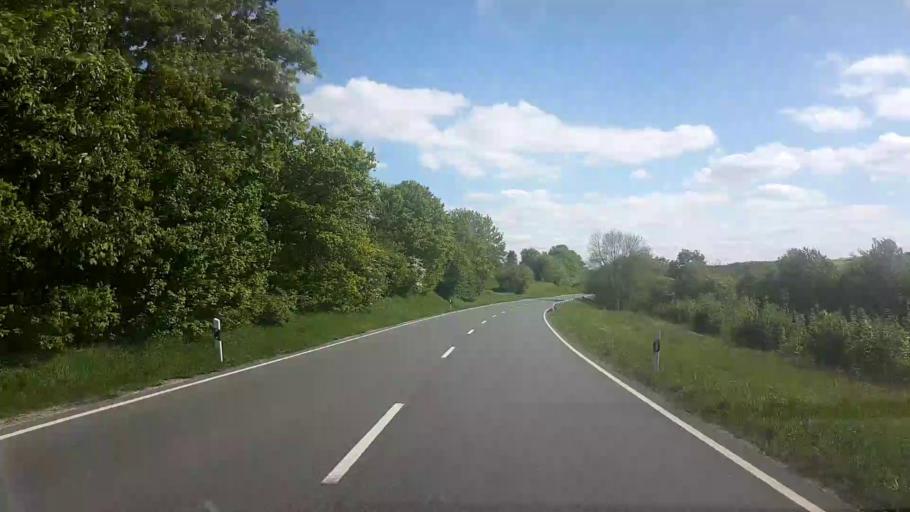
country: DE
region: Bavaria
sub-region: Regierungsbezirk Unterfranken
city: Untermerzbach
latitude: 50.0720
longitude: 10.8649
